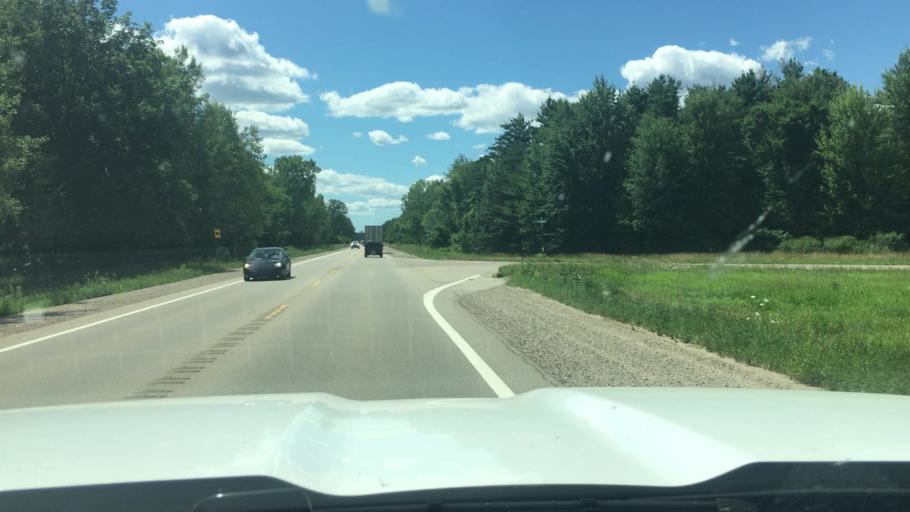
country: US
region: Michigan
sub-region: Kent County
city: Cedar Springs
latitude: 43.1760
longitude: -85.4696
